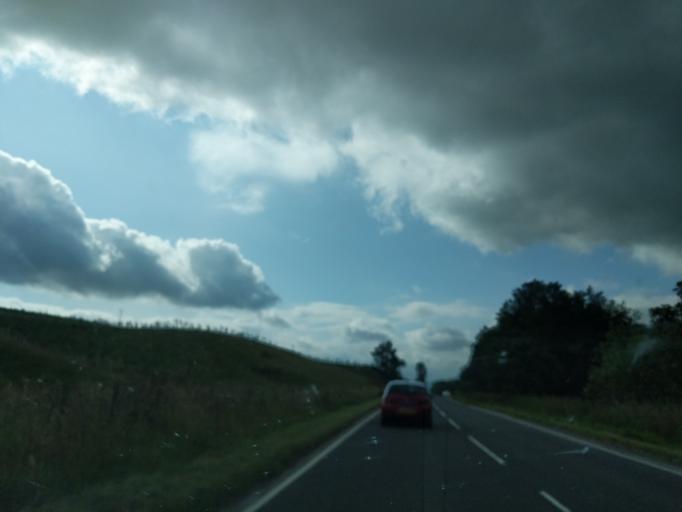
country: GB
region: Scotland
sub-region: Midlothian
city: Penicuik
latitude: 55.7549
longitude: -3.2064
